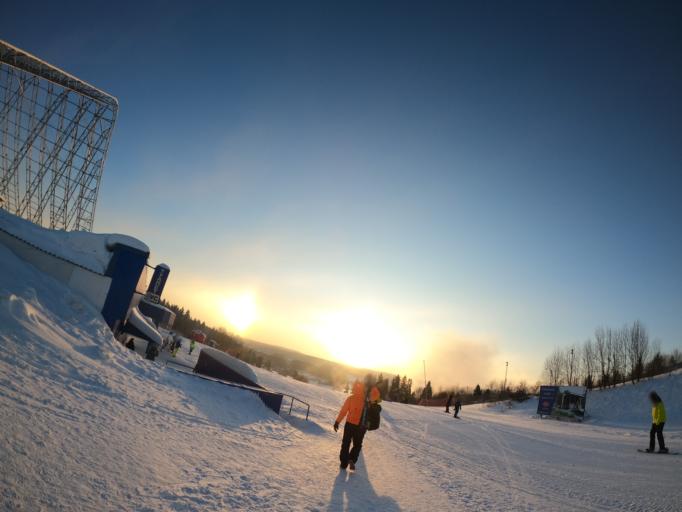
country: RU
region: Moskovskaya
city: Dedenevo
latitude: 56.2769
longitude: 37.5655
